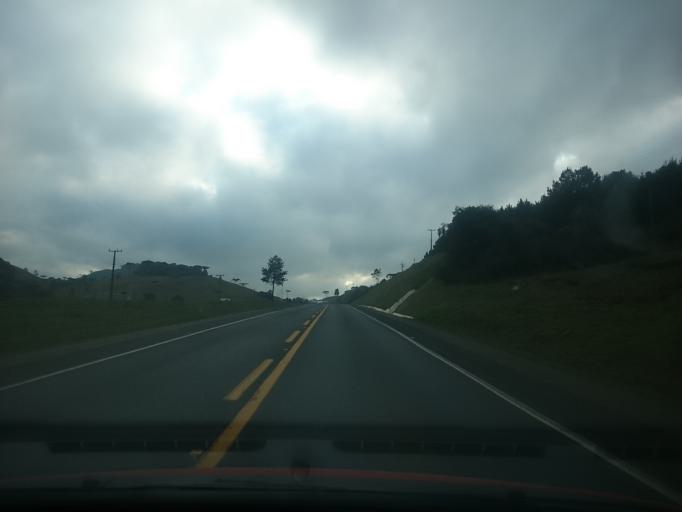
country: BR
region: Santa Catarina
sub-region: Lages
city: Lages
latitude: -27.8587
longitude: -50.3875
